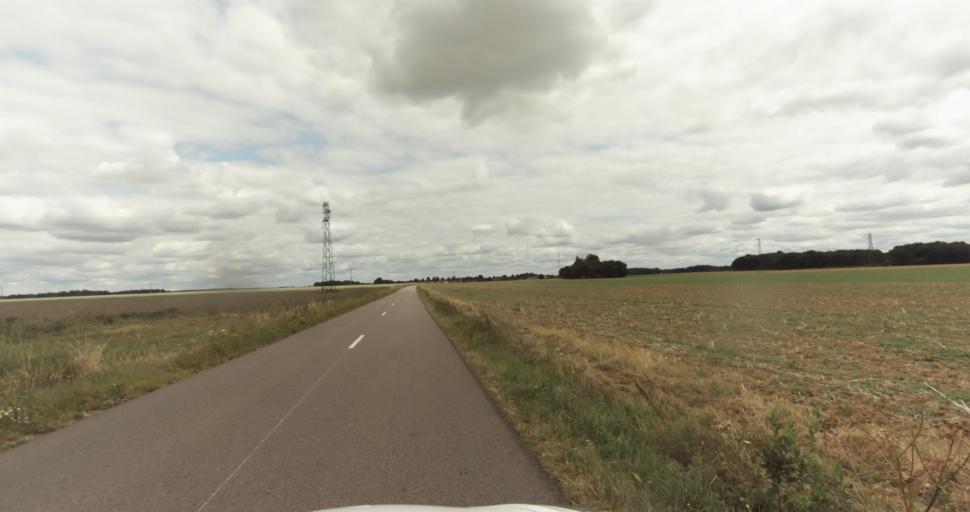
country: FR
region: Centre
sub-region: Departement d'Eure-et-Loir
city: Saint-Remy-sur-Avre
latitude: 48.7980
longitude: 1.2501
